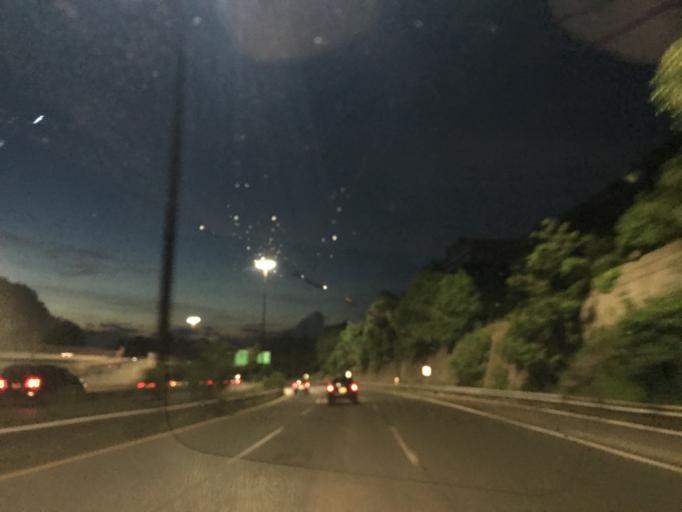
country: US
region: New Jersey
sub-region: Bergen County
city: Fort Lee
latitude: 40.8623
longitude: -73.9744
